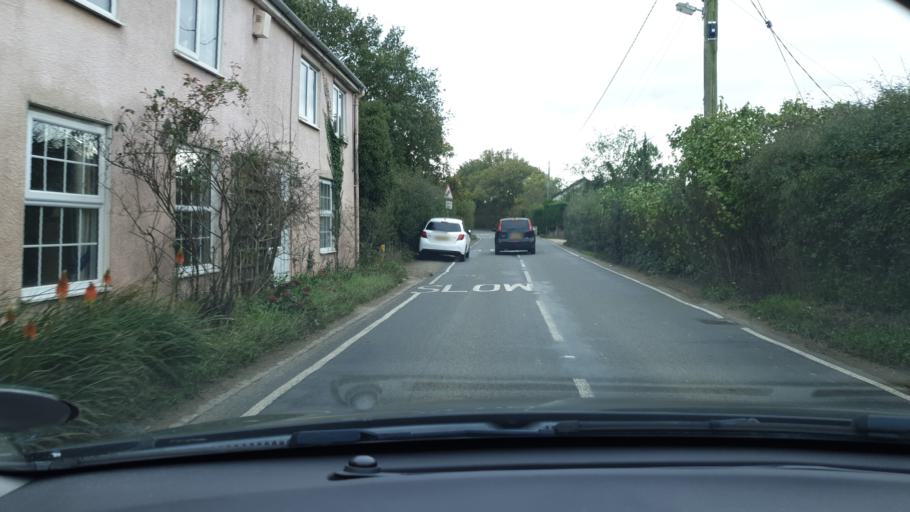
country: GB
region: England
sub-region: Essex
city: Great Bentley
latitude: 51.8517
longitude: 1.0351
